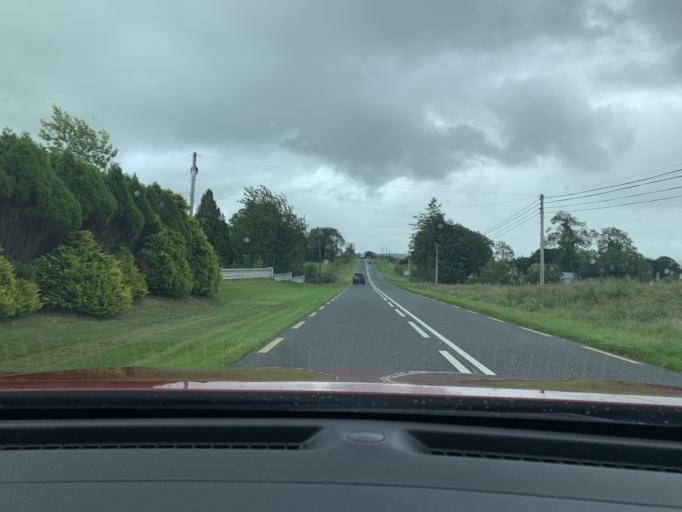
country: IE
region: Ulster
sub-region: County Donegal
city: Raphoe
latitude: 54.7995
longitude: -7.5735
